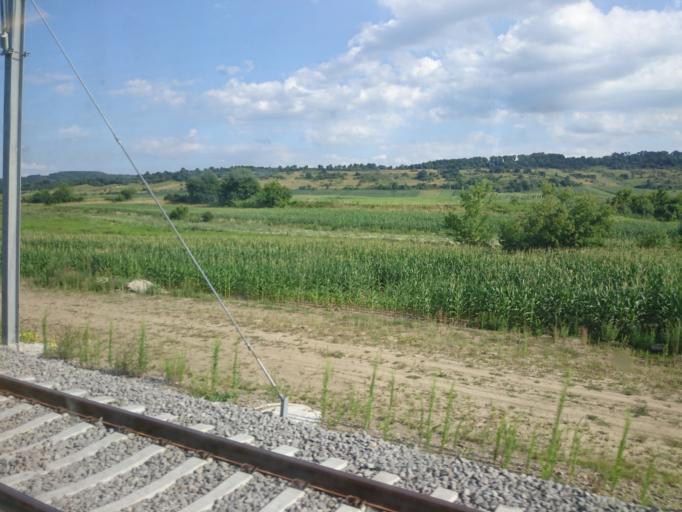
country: RO
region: Sibiu
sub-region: Comuna Laslea
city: Laslea
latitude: 46.2207
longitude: 24.6452
